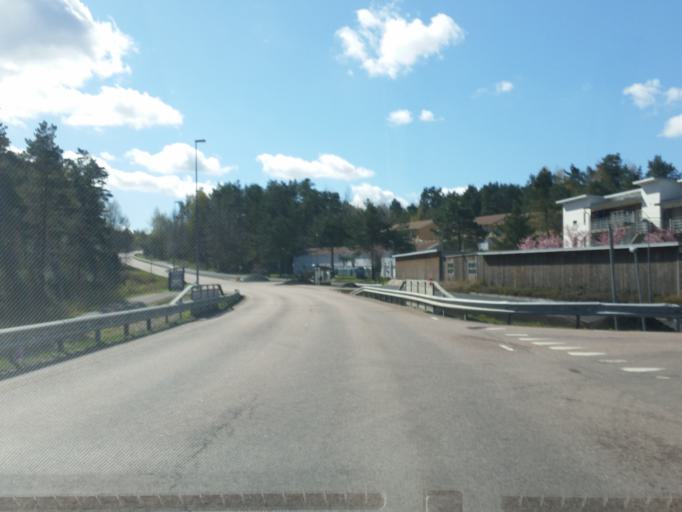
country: SE
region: Vaestra Goetaland
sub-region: Partille Kommun
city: Furulund
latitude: 57.7308
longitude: 12.1331
